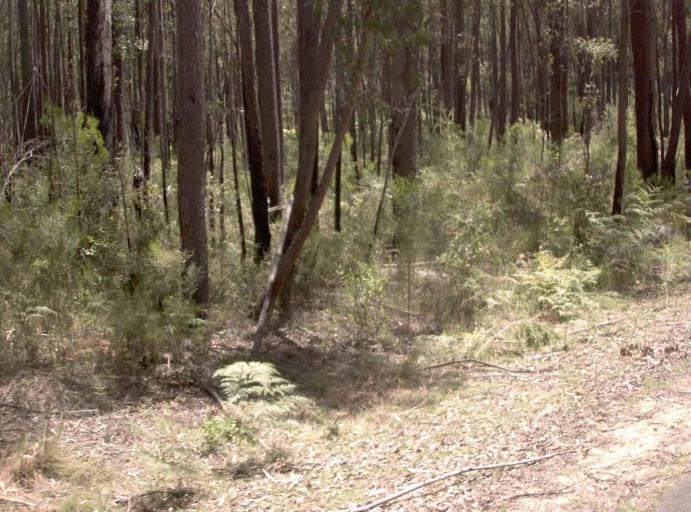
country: AU
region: New South Wales
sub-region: Bombala
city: Bombala
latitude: -37.5624
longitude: 148.9456
